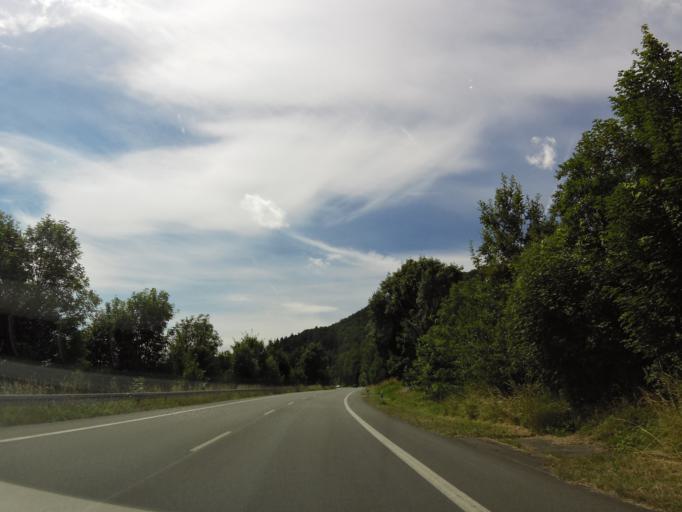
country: DE
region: North Rhine-Westphalia
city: Beverungen
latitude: 51.6535
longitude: 9.3710
